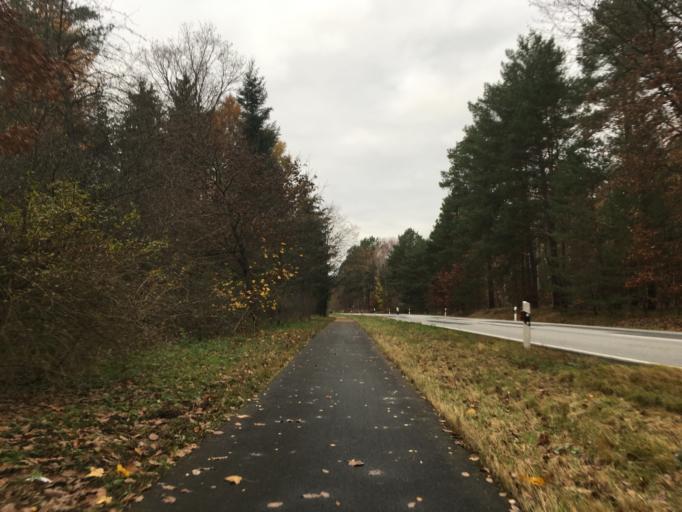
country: DE
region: Brandenburg
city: Mullrose
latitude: 52.2202
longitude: 14.4453
